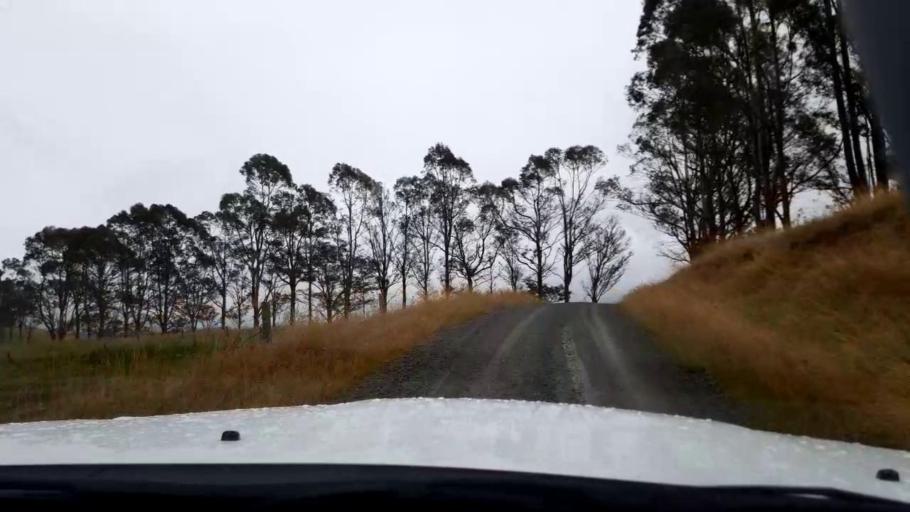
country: NZ
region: Canterbury
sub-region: Timaru District
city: Pleasant Point
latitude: -44.1727
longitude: 171.1046
